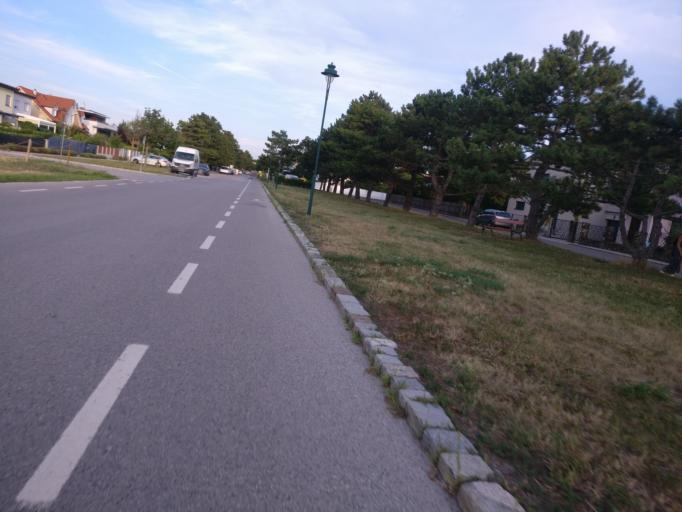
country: AT
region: Lower Austria
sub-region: Politischer Bezirk Modling
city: Laxenburg
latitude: 48.0708
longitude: 16.3494
